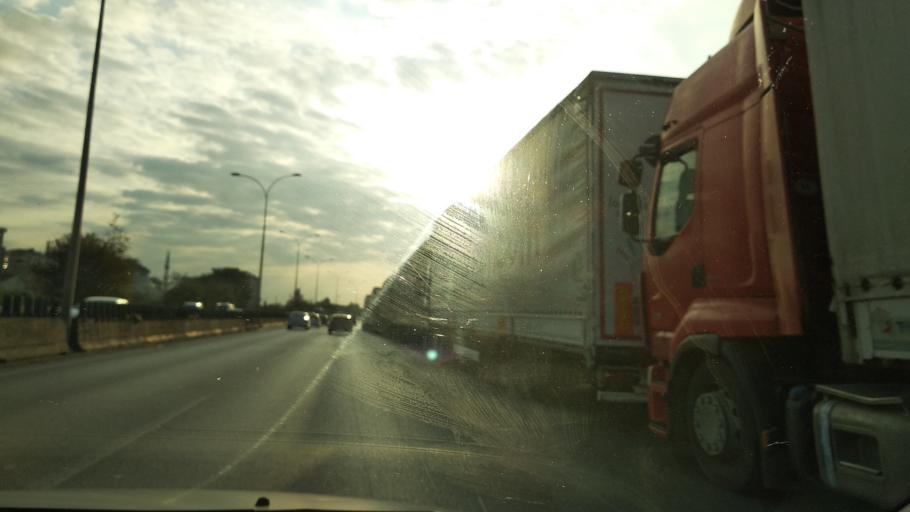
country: TR
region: Istanbul
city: Pendik
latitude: 40.8711
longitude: 29.2864
